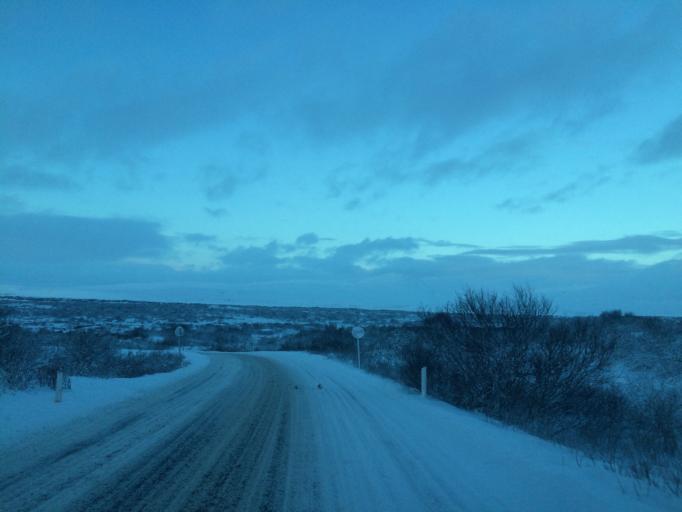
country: IS
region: South
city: Hveragerdi
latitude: 64.2600
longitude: -21.0385
